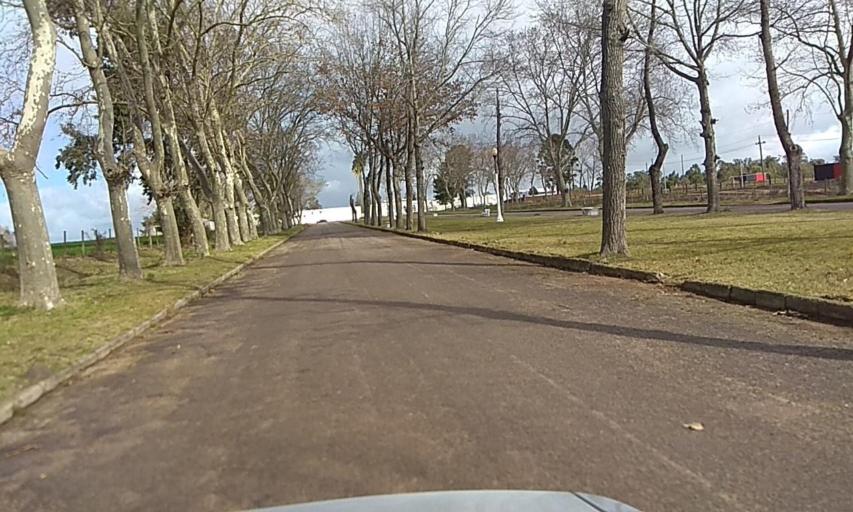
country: UY
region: Florida
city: Florida
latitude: -34.1073
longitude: -56.2269
